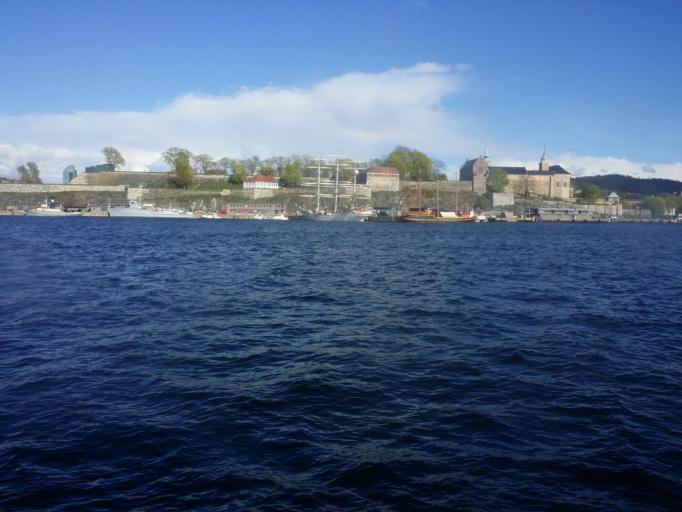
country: NO
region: Oslo
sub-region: Oslo
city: Oslo
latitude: 59.9084
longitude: 10.7281
